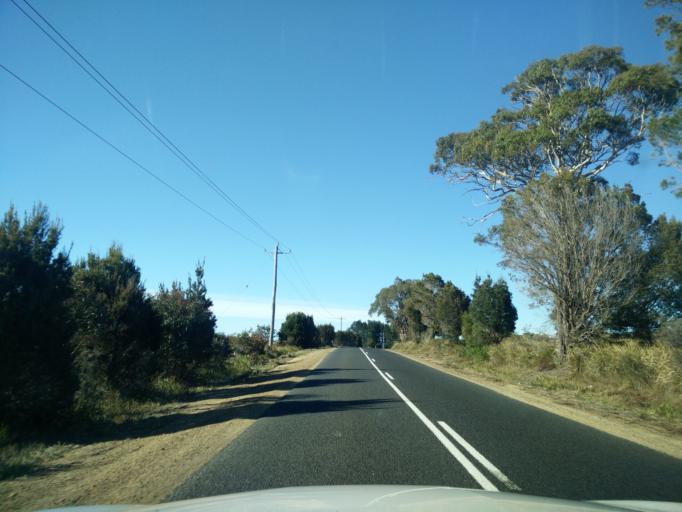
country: AU
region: Tasmania
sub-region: Break O'Day
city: St Helens
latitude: -41.9314
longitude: 148.2271
